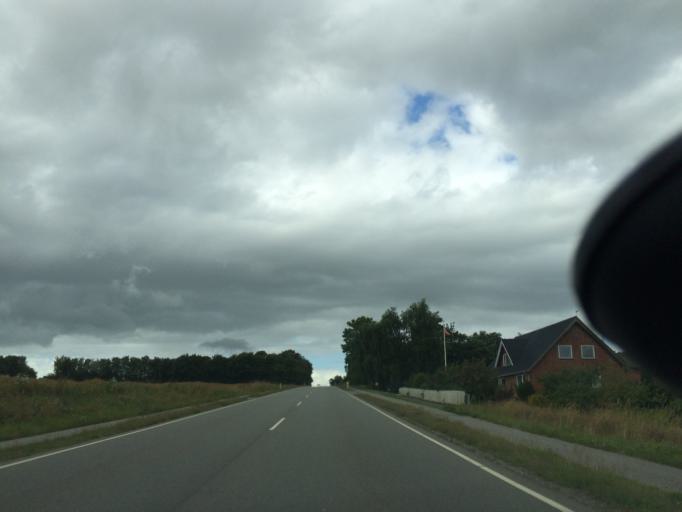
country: DK
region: Central Jutland
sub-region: Skanderborg Kommune
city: Galten
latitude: 56.1483
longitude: 9.8853
